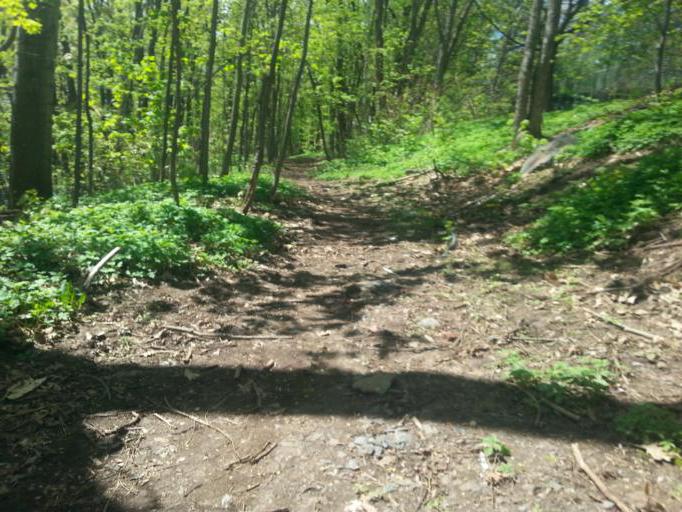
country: CA
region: Quebec
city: Quebec
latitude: 46.7693
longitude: -71.2594
